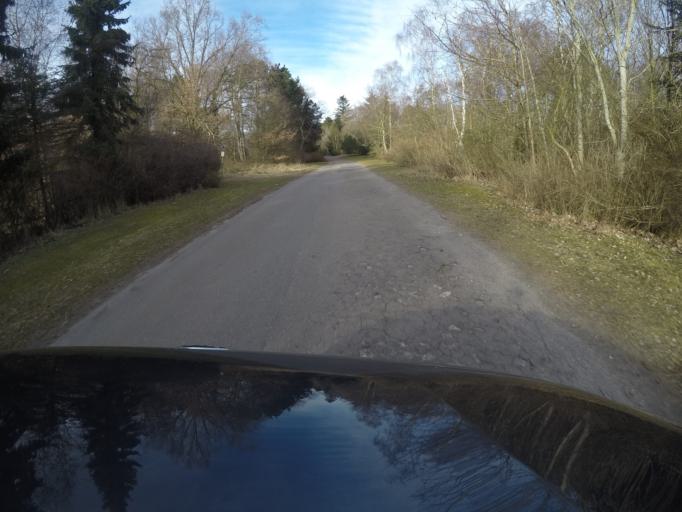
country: DK
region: Capital Region
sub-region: Halsnaes Kommune
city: Liseleje
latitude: 55.9941
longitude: 11.9306
